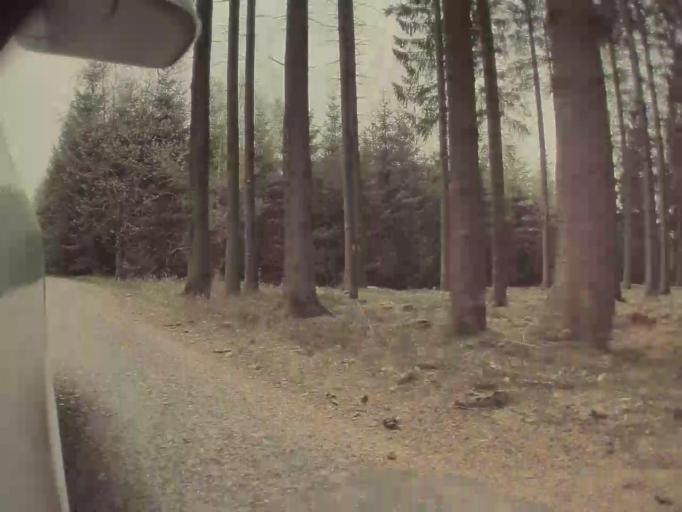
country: BE
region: Wallonia
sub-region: Province du Luxembourg
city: La Roche-en-Ardenne
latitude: 50.2356
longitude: 5.5960
